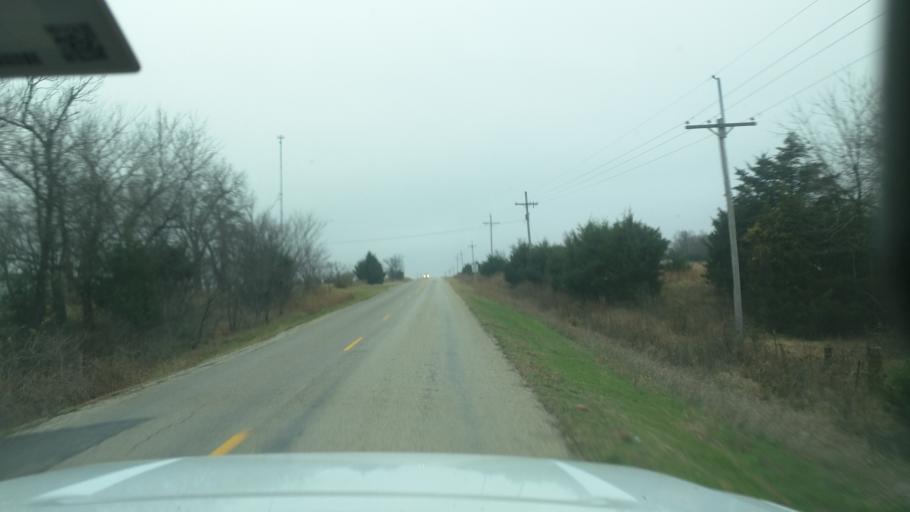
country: US
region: Kansas
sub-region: Morris County
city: Council Grove
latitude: 38.6360
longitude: -96.2614
